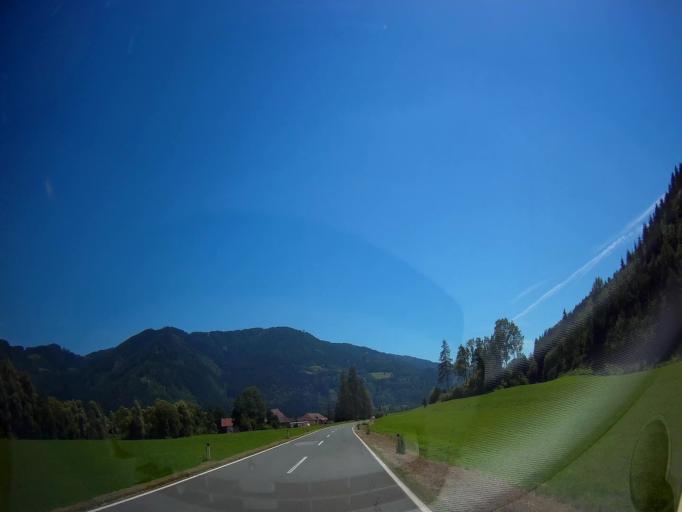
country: AT
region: Carinthia
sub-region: Politischer Bezirk Sankt Veit an der Glan
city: Friesach
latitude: 46.9422
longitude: 14.4195
